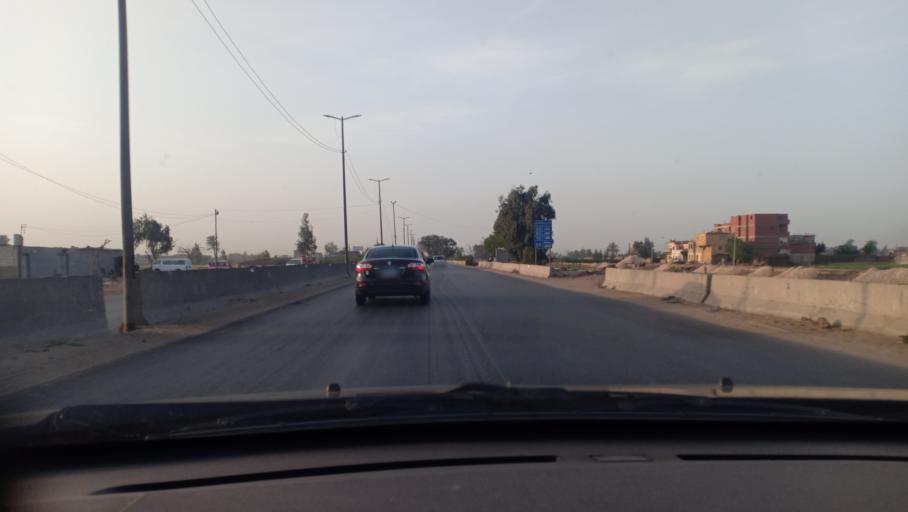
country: EG
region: Muhafazat al Minufiyah
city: Quwaysina
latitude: 30.5806
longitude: 31.2737
